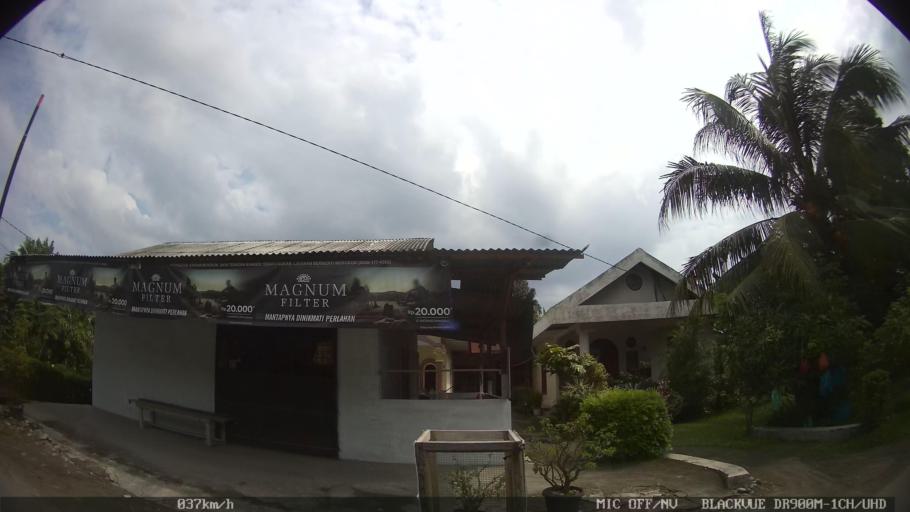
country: ID
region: North Sumatra
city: Sunggal
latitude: 3.6358
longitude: 98.5977
